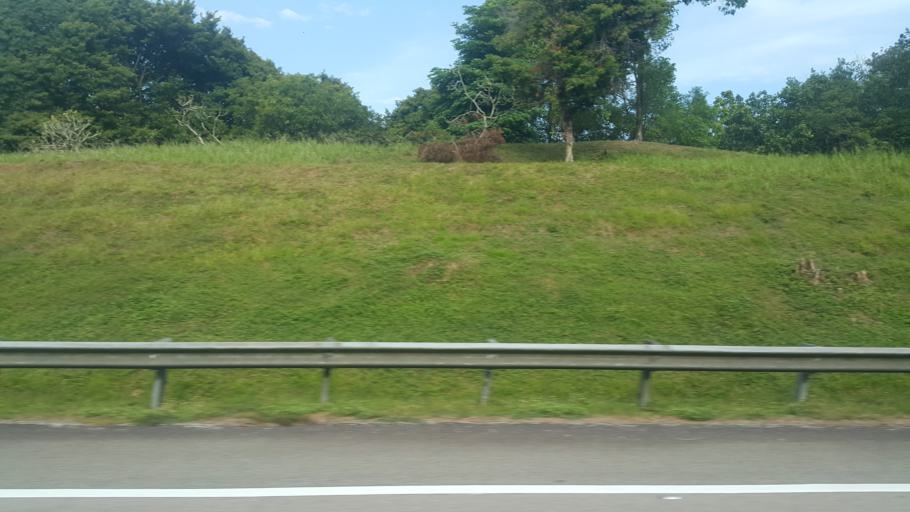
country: MY
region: Johor
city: Taman Senai
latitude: 1.5932
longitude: 103.6123
